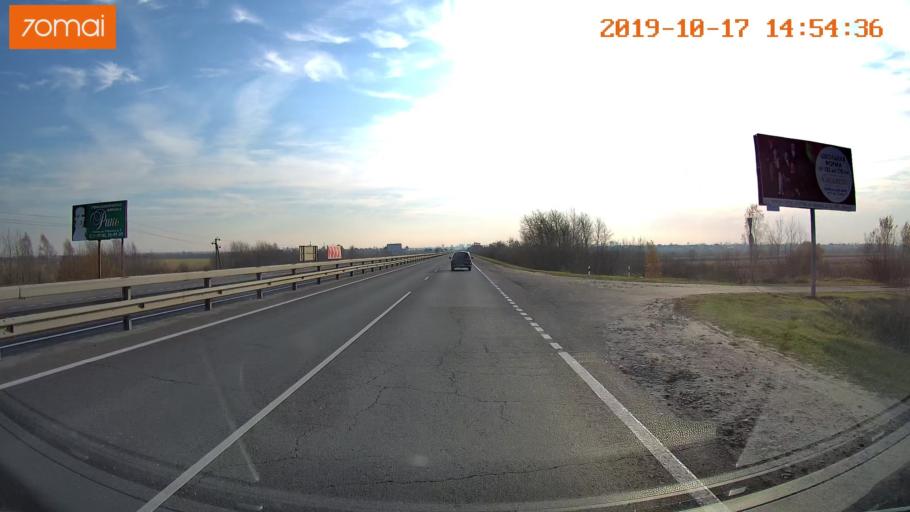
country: RU
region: Rjazan
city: Polyany
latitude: 54.6793
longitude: 39.8307
